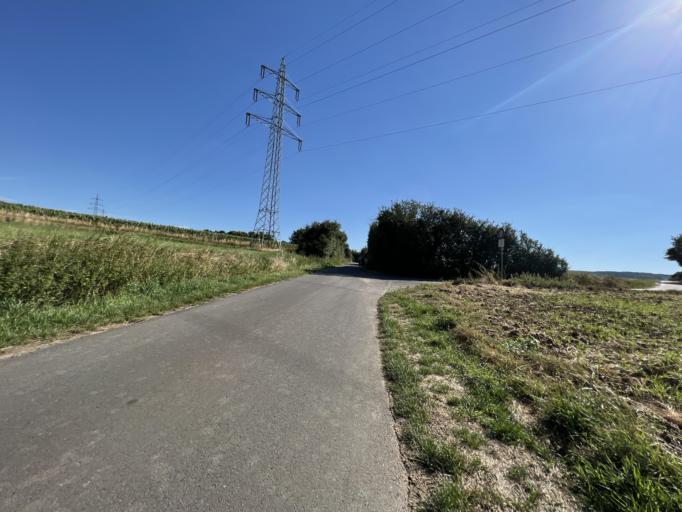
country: DE
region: North Rhine-Westphalia
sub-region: Regierungsbezirk Koln
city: Kreuzau
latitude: 50.7691
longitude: 6.4418
